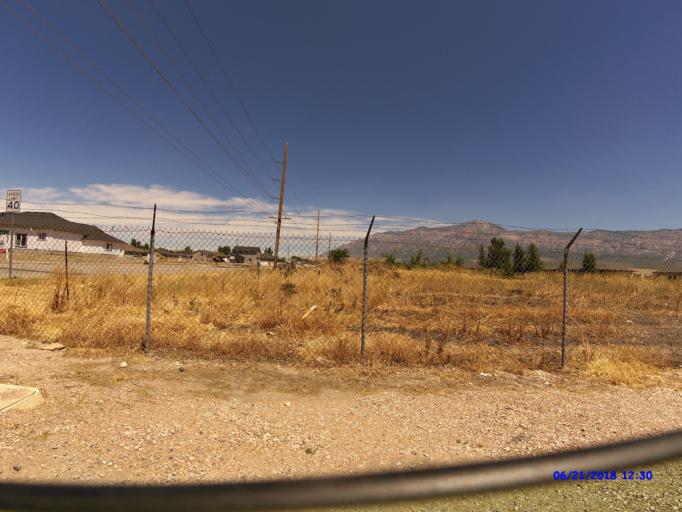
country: US
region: Utah
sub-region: Weber County
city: Harrisville
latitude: 41.2759
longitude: -112.0083
